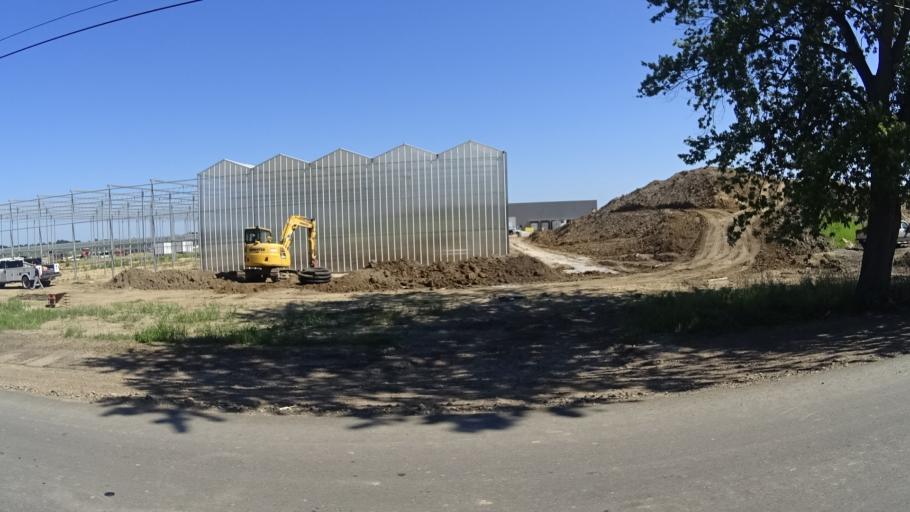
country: US
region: Ohio
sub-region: Erie County
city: Huron
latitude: 41.3892
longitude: -82.5921
